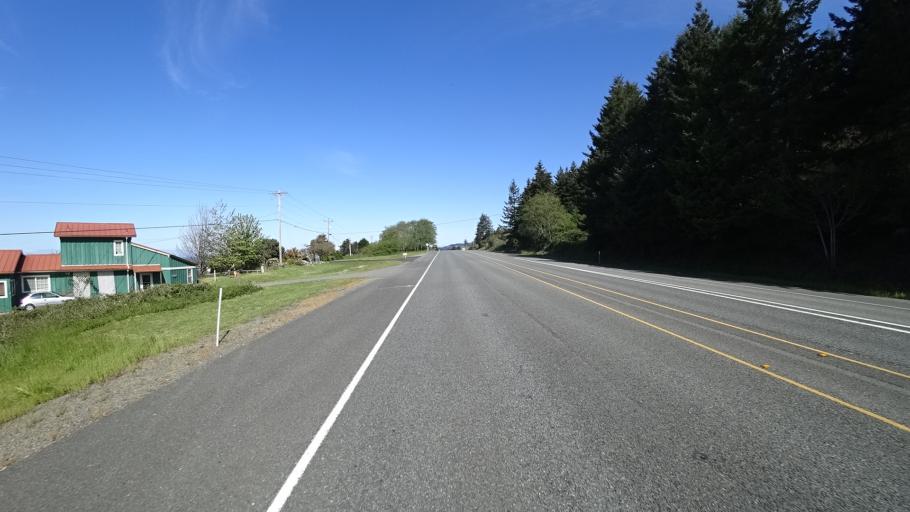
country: US
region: Oregon
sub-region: Curry County
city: Harbor
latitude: 42.0236
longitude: -124.2277
